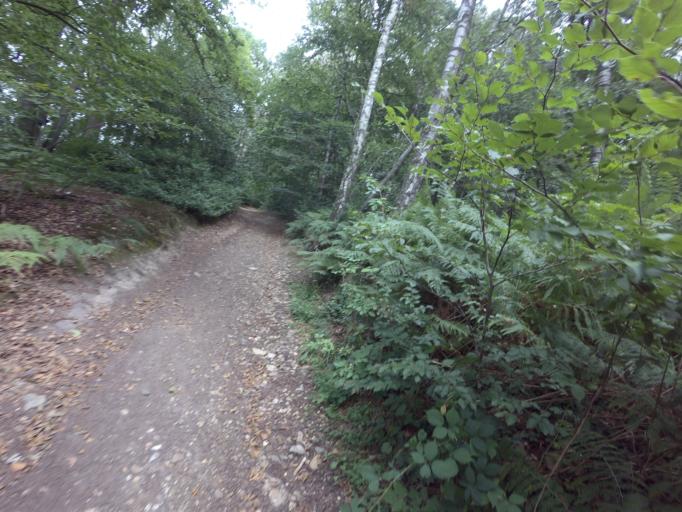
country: NL
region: Limburg
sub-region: Valkenburg aan de Geul
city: Schin op Geul
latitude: 50.7837
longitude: 5.8881
